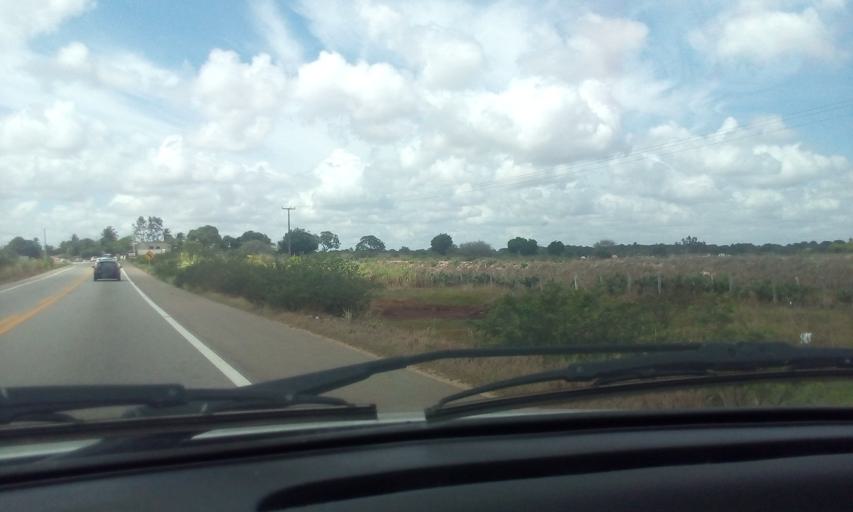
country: BR
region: Rio Grande do Norte
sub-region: Macaiba
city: Macaiba
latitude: -5.9215
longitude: -35.5352
